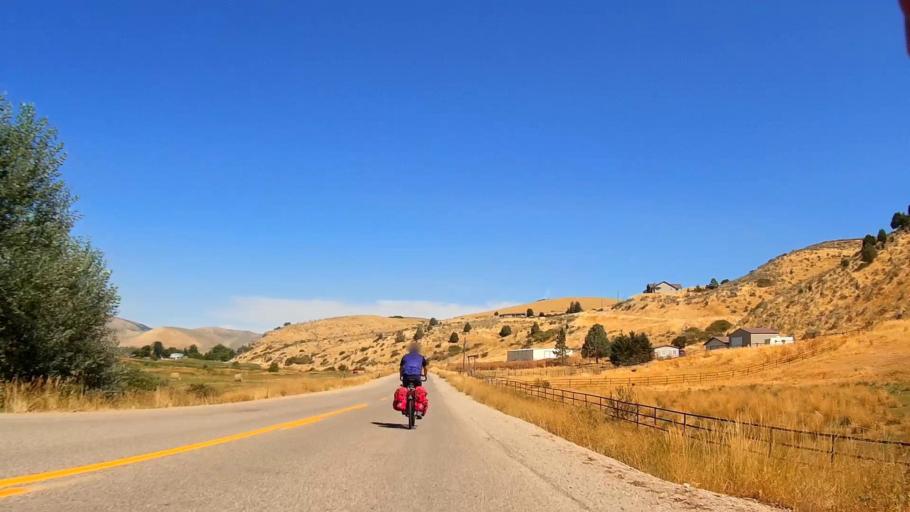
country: US
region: Idaho
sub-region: Bannock County
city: Pocatello
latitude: 42.7568
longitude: -112.2153
